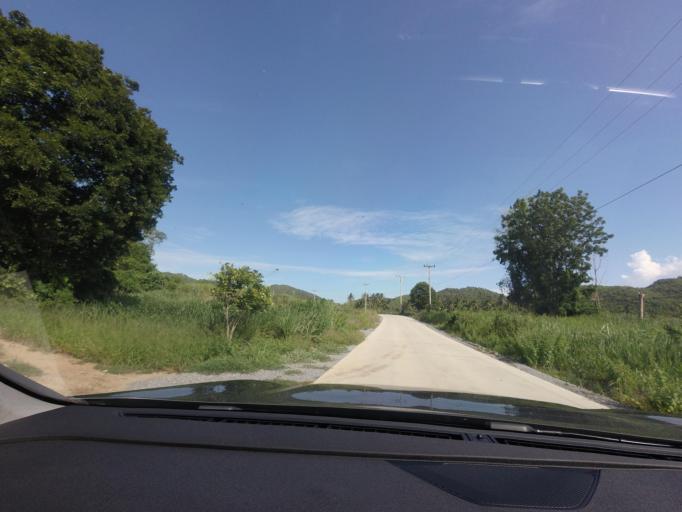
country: TH
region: Prachuap Khiri Khan
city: Pran Buri
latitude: 12.4729
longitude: 99.9383
